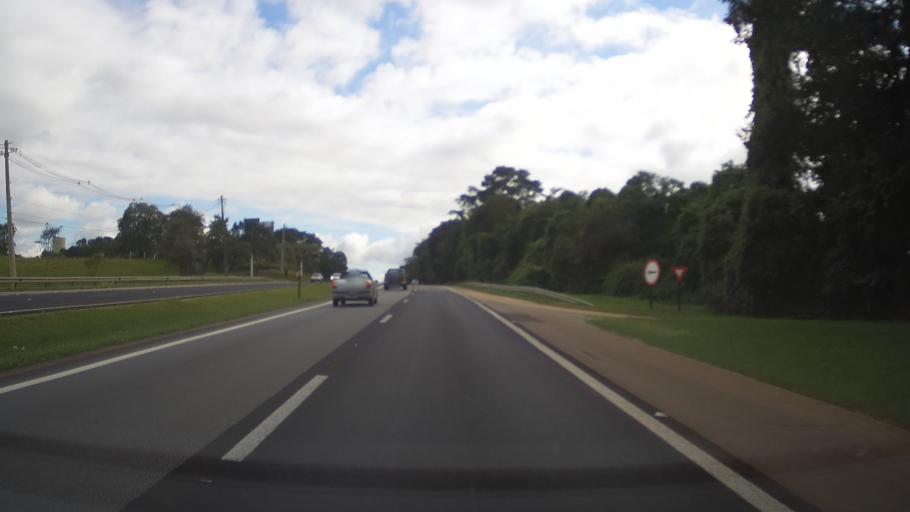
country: BR
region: Sao Paulo
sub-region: Itupeva
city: Itupeva
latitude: -23.2156
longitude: -47.0193
